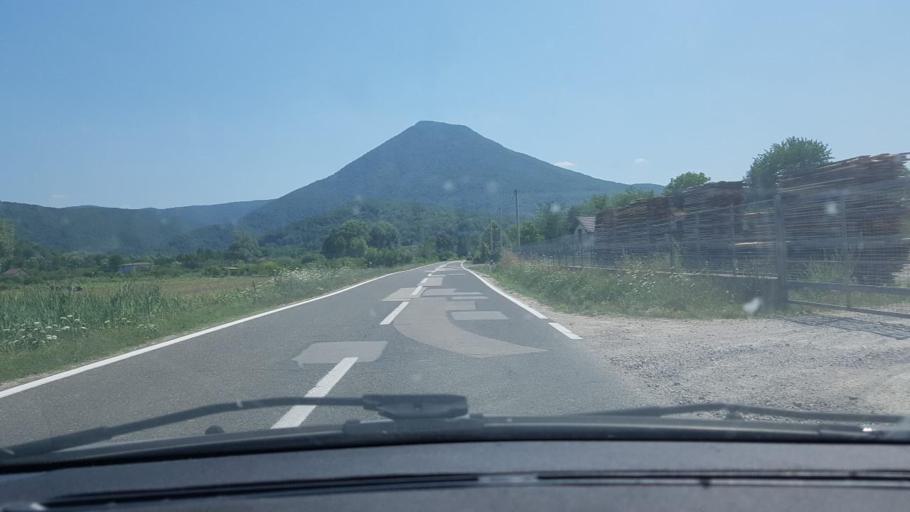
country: BA
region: Federation of Bosnia and Herzegovina
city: Bihac
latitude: 44.7594
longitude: 15.9445
